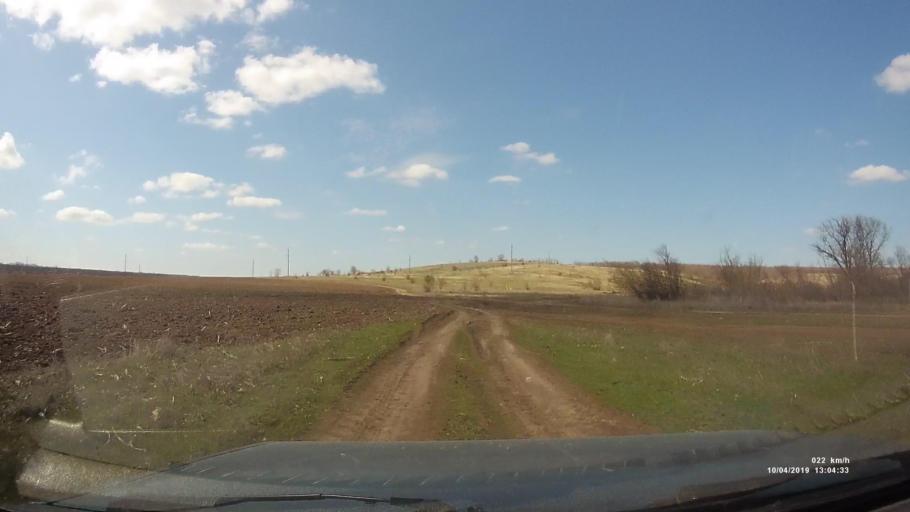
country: RU
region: Rostov
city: Masalovka
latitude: 48.3857
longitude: 40.2357
